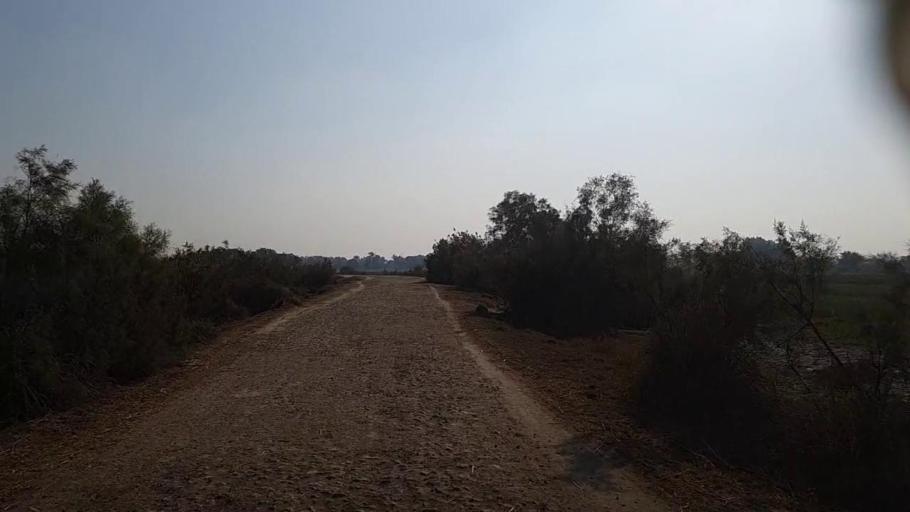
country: PK
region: Sindh
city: Mirpur Mathelo
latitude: 27.8997
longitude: 69.6067
